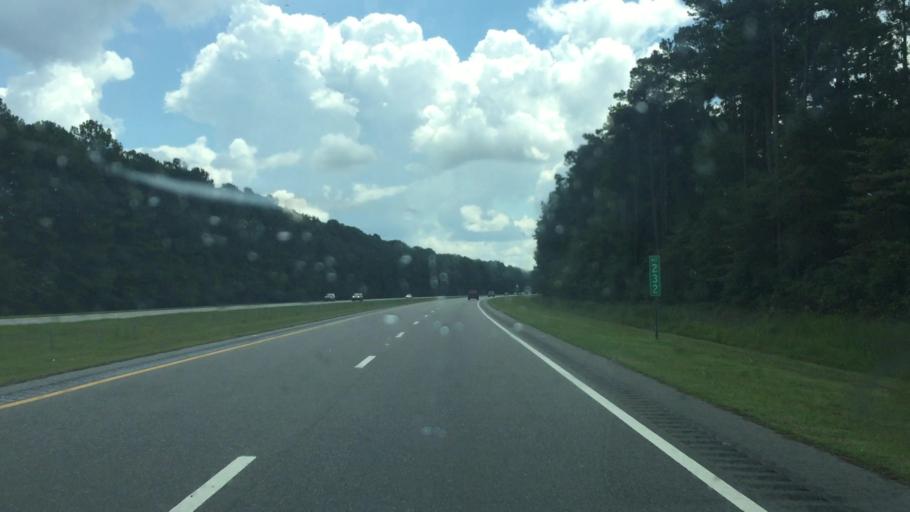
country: US
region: North Carolina
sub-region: Columbus County
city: Chadbourn
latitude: 34.3785
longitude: -78.8513
